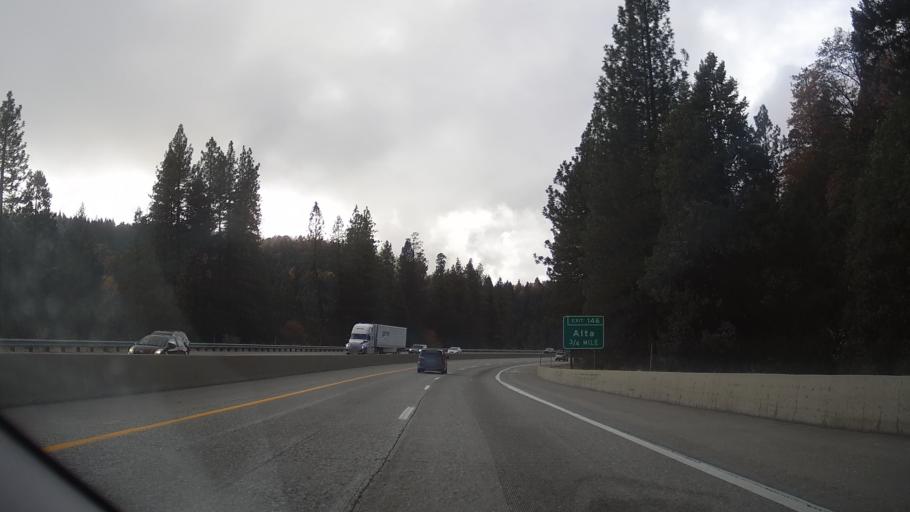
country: US
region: California
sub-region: Placer County
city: Foresthill
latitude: 39.2042
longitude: -120.7954
